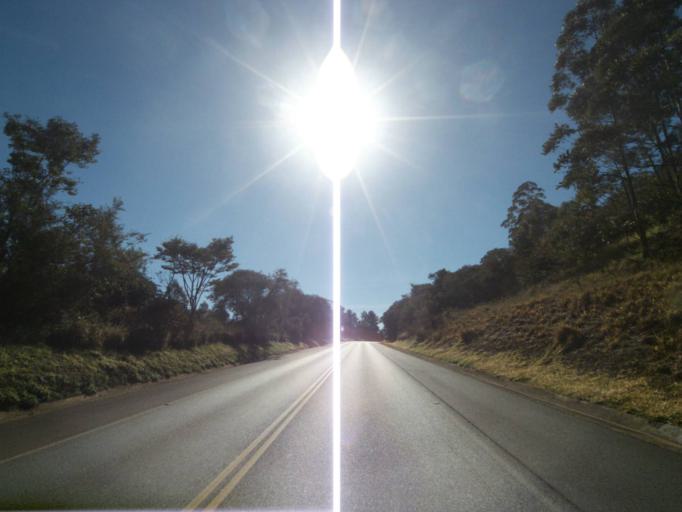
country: BR
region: Parana
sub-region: Tibagi
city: Tibagi
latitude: -24.4097
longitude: -50.3540
